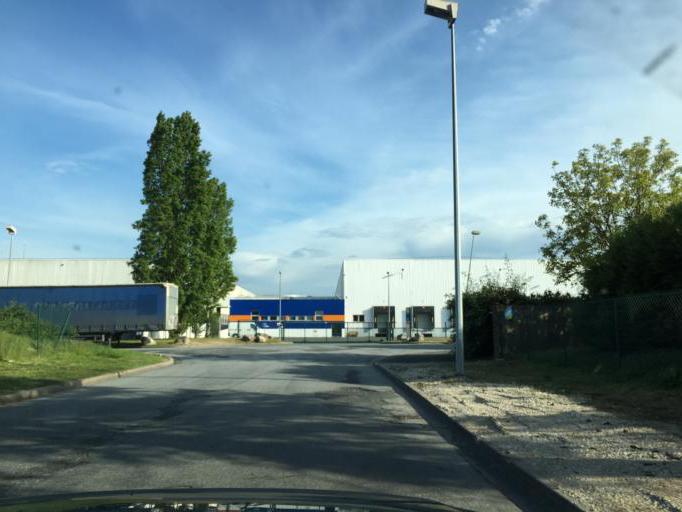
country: FR
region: Centre
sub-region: Departement du Loiret
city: Ormes
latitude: 47.9463
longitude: 1.8285
